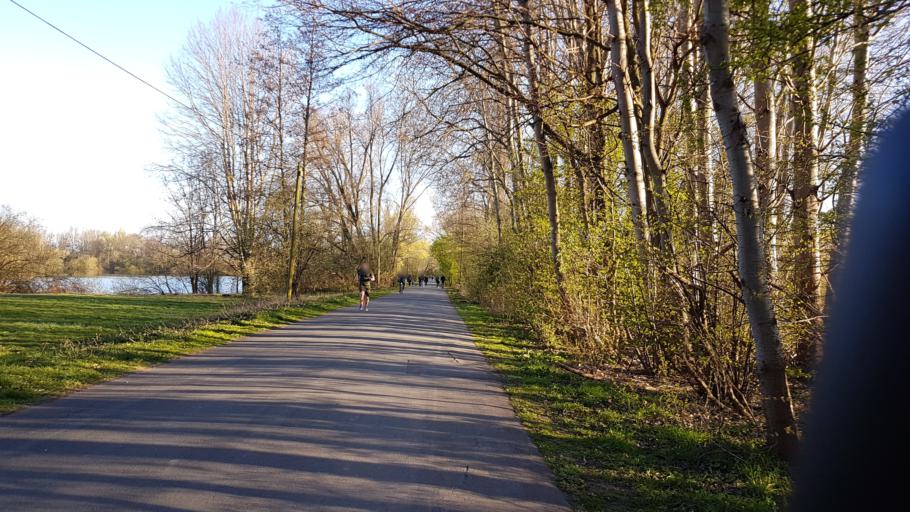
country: DE
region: Lower Saxony
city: Hannover
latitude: 52.3430
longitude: 9.7399
